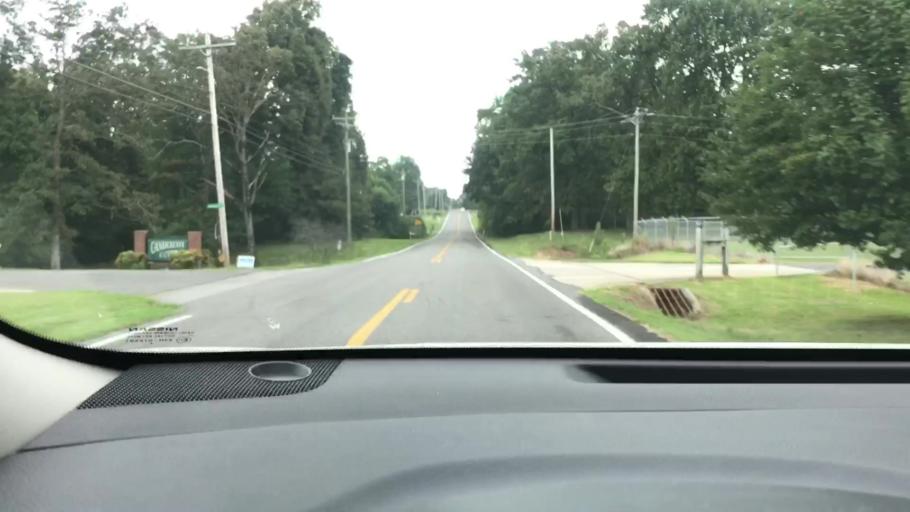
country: US
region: Kentucky
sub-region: Calloway County
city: Murray
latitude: 36.6858
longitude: -88.2988
